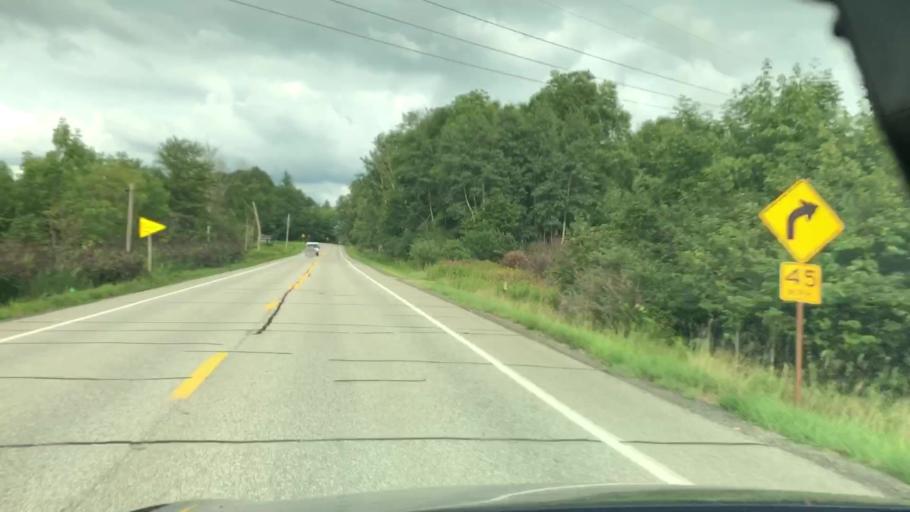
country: US
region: Pennsylvania
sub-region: Erie County
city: Northwest Harborcreek
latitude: 42.0604
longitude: -79.8812
